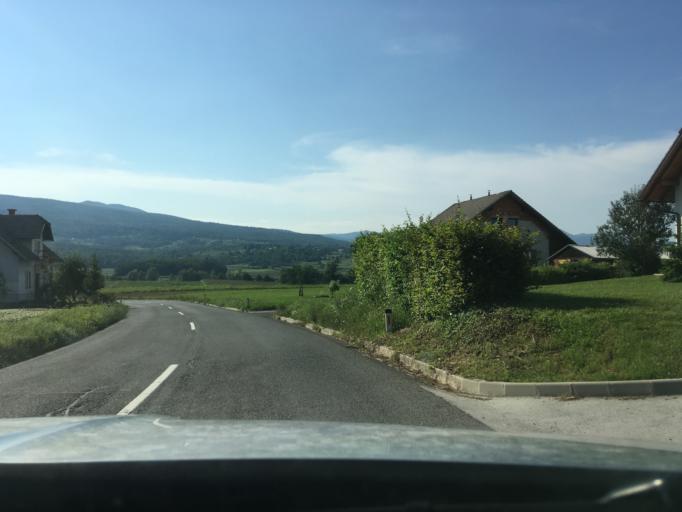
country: SI
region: Crnomelj
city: Crnomelj
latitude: 45.5205
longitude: 15.1744
